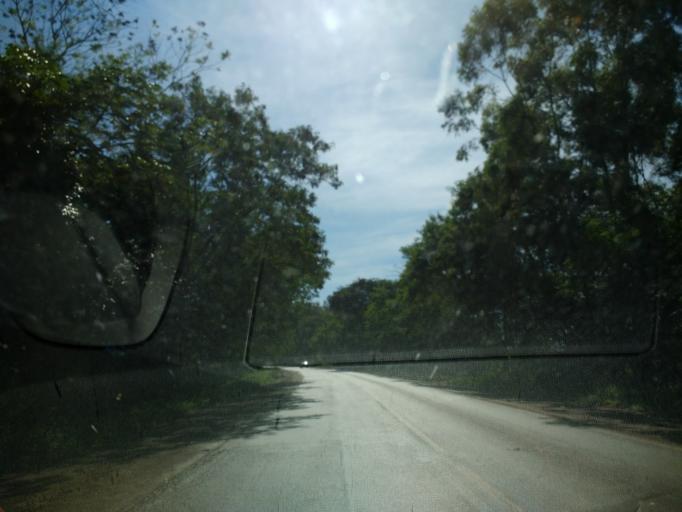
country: BR
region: Parana
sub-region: Umuarama
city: Umuarama
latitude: -23.8794
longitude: -53.3956
